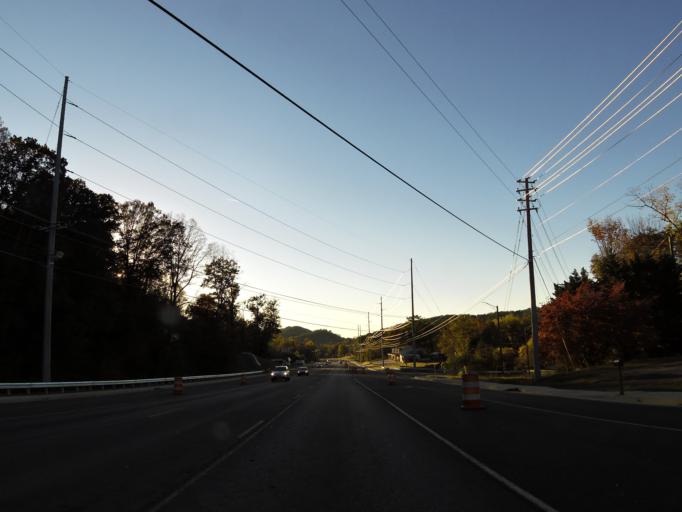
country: US
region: Tennessee
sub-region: Knox County
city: Knoxville
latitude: 35.9877
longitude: -84.0390
